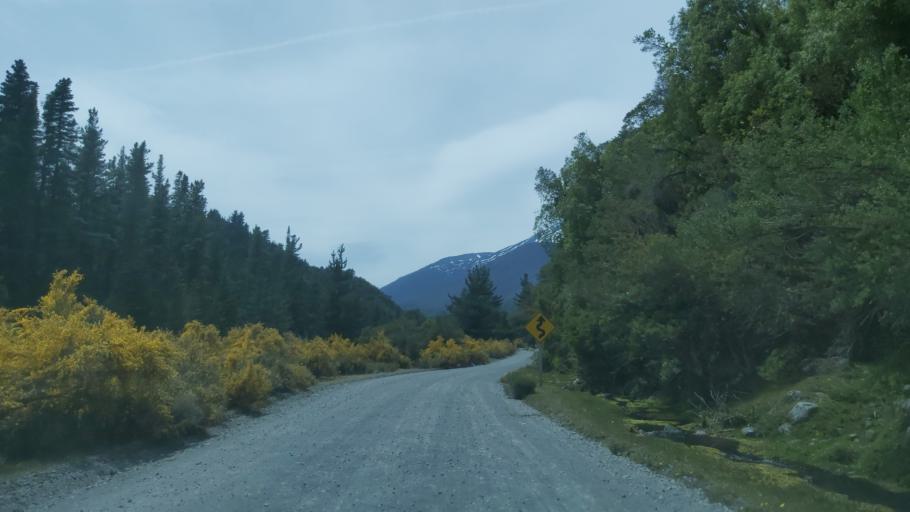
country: AR
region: Neuquen
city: Las Ovejas
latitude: -37.3968
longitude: -71.4528
